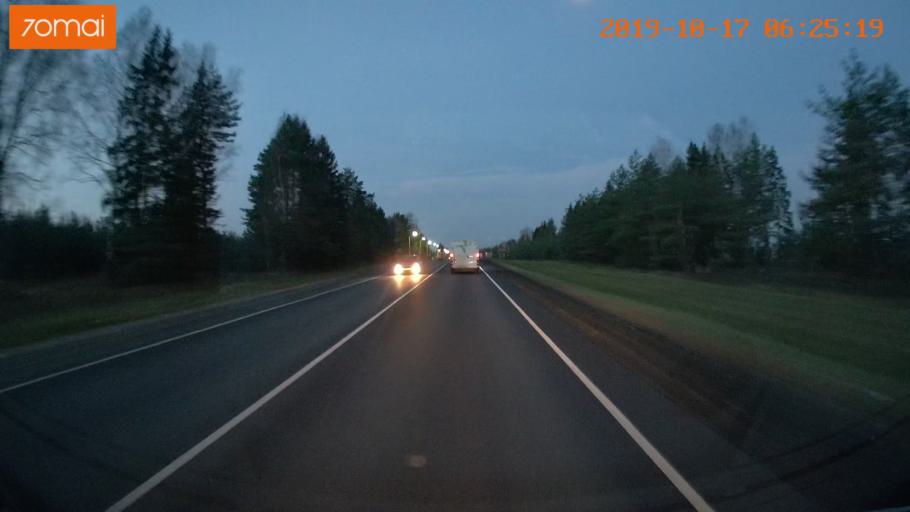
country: RU
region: Ivanovo
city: Lezhnevo
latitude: 56.7694
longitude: 40.8094
